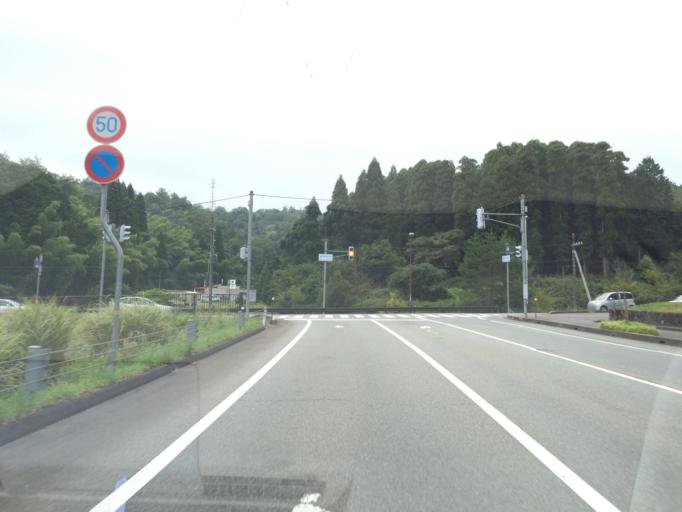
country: JP
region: Hyogo
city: Toyooka
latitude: 35.5267
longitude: 134.8088
